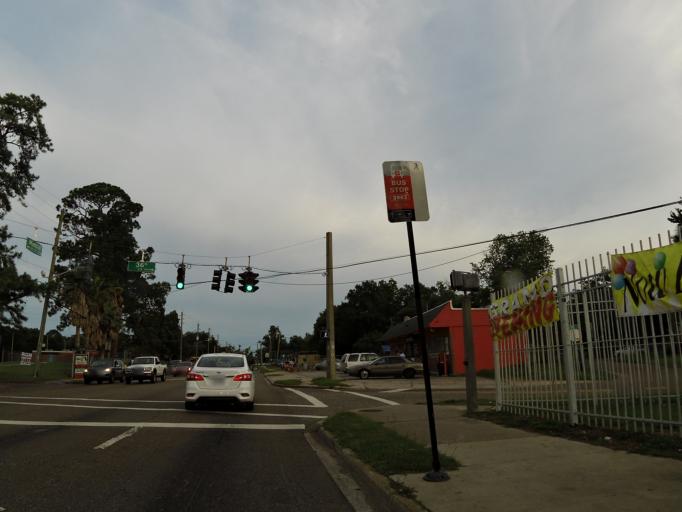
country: US
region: Florida
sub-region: Duval County
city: Jacksonville
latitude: 30.3672
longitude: -81.6814
